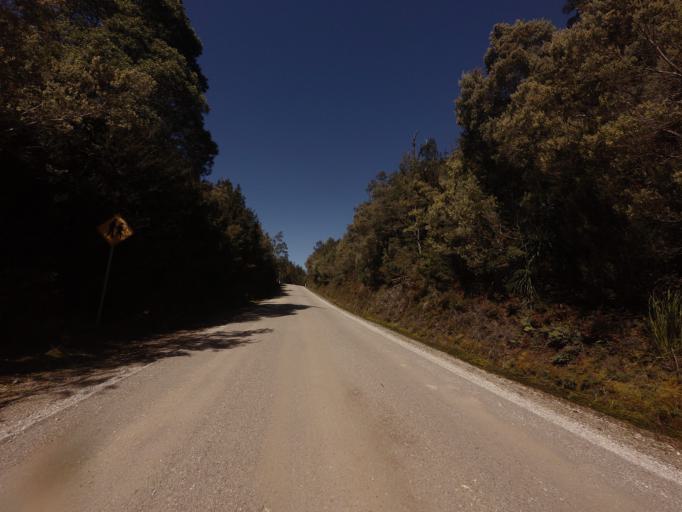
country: AU
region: Tasmania
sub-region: Huon Valley
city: Geeveston
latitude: -42.8312
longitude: 146.3852
